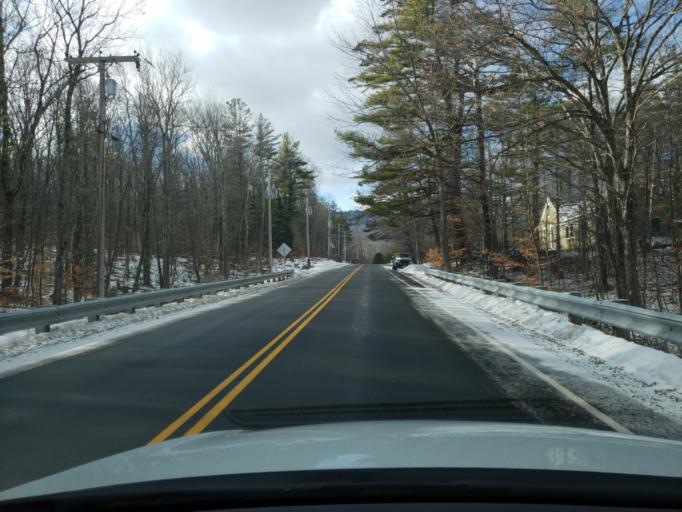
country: US
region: New Hampshire
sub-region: Hillsborough County
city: Deering
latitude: 43.0092
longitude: -71.8456
